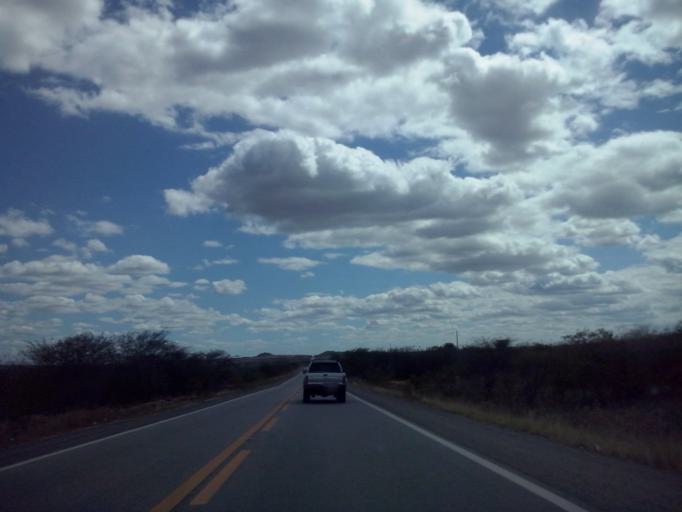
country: BR
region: Paraiba
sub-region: Soledade
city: Soledade
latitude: -7.0386
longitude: -36.4219
